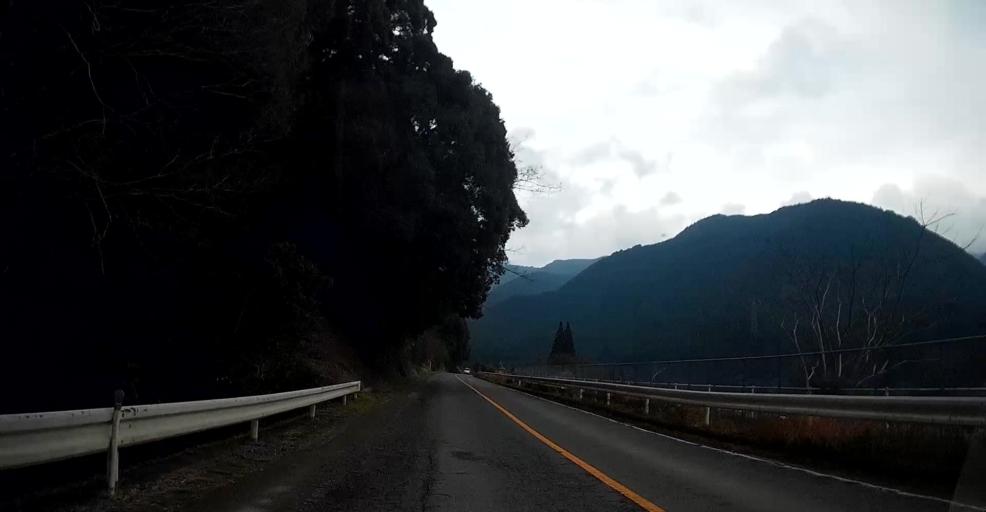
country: JP
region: Kumamoto
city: Matsubase
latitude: 32.6156
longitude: 130.8423
